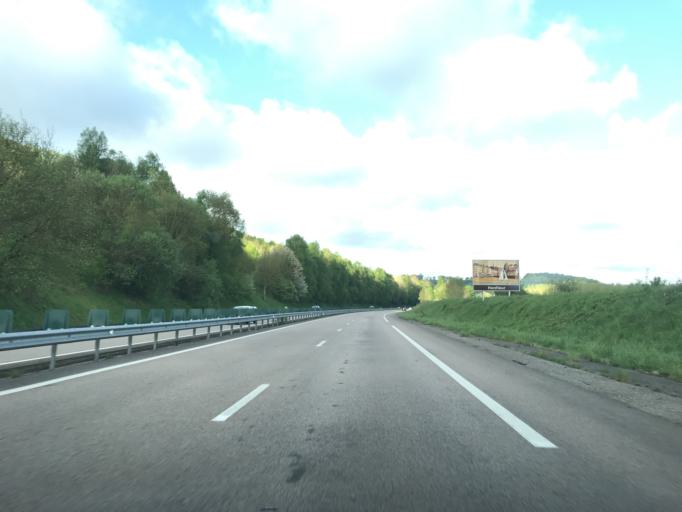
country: FR
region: Haute-Normandie
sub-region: Departement de l'Eure
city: Toutainville
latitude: 49.3517
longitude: 0.4450
